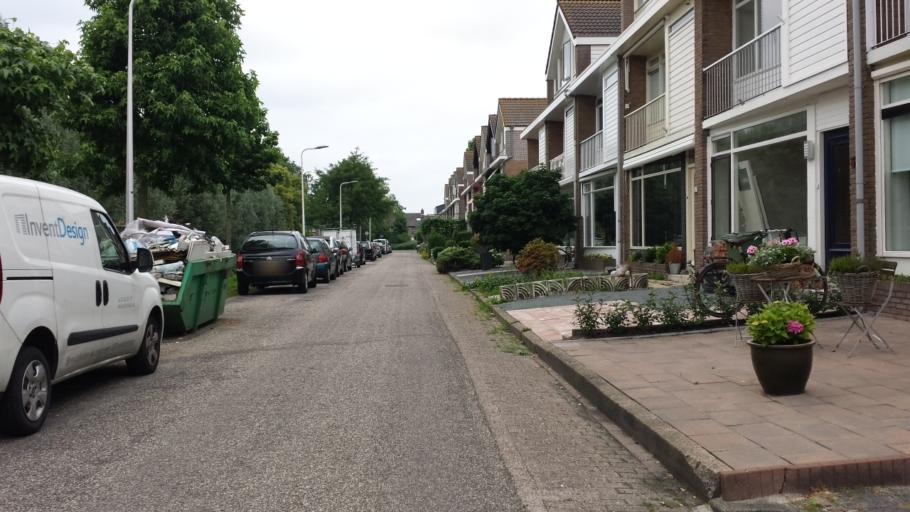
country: NL
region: South Holland
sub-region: Bodegraven-Reeuwijk
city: Reeuwijk
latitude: 52.0480
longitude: 4.7228
